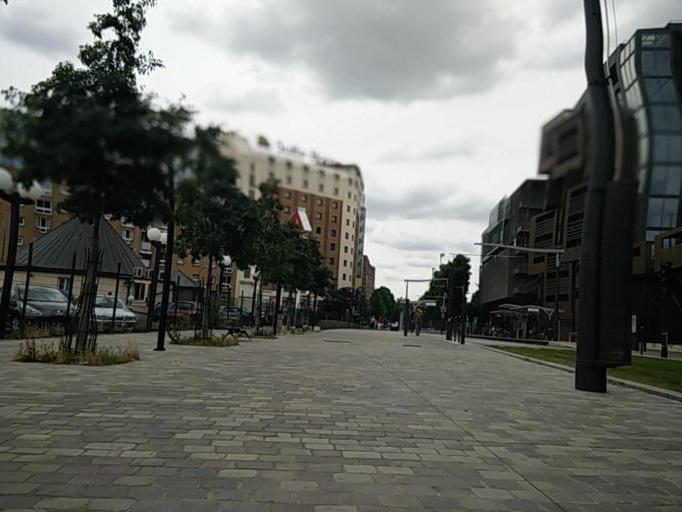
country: FR
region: Ile-de-France
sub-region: Departement de Seine-Saint-Denis
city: Le Pre-Saint-Gervais
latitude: 48.8944
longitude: 2.3976
